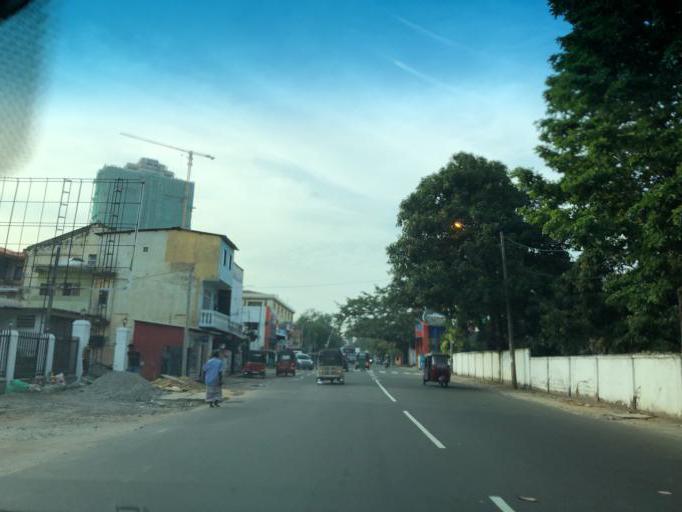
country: LK
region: Western
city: Pita Kotte
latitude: 6.8911
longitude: 79.8793
